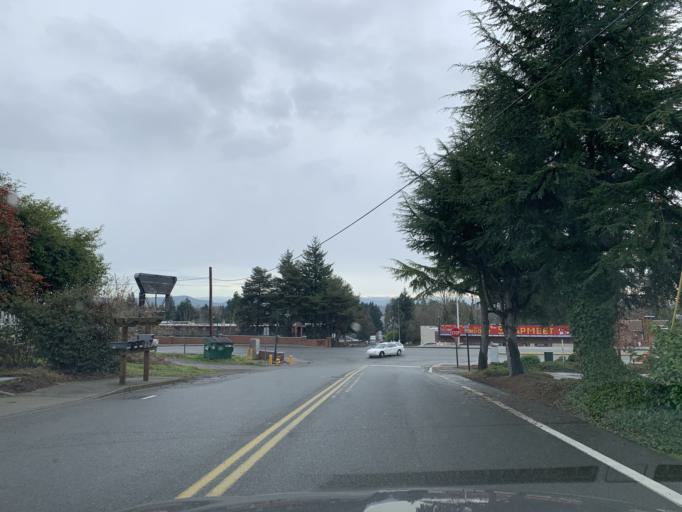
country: US
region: Washington
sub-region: King County
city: Riverton
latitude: 47.4706
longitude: -122.2870
